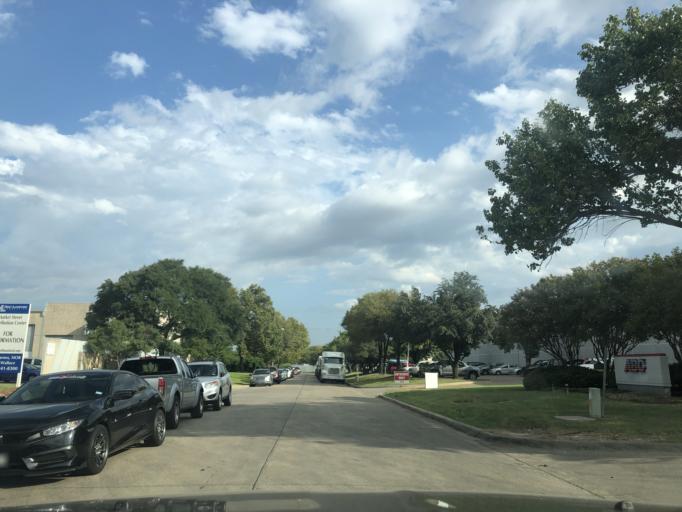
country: US
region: Texas
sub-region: Dallas County
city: Garland
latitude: 32.8844
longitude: -96.6684
